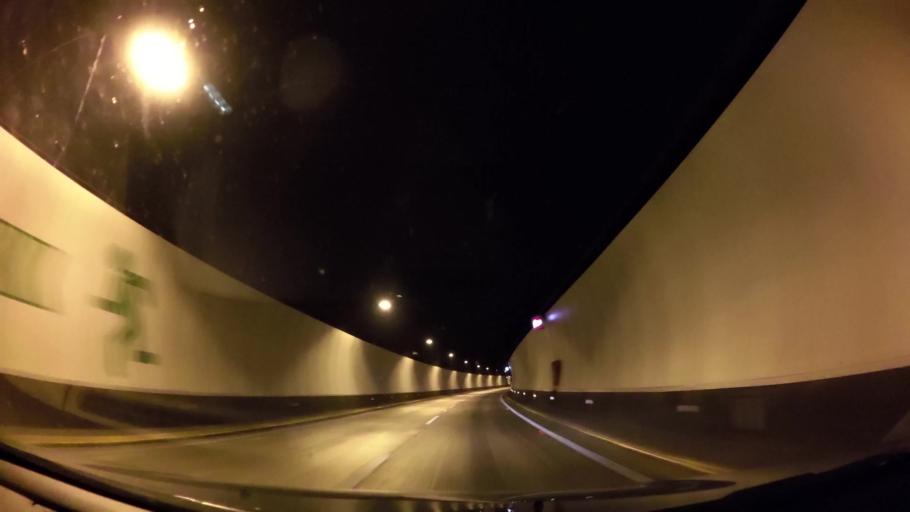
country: CL
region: Santiago Metropolitan
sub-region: Provincia de Santiago
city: Santiago
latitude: -33.4040
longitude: -70.6139
